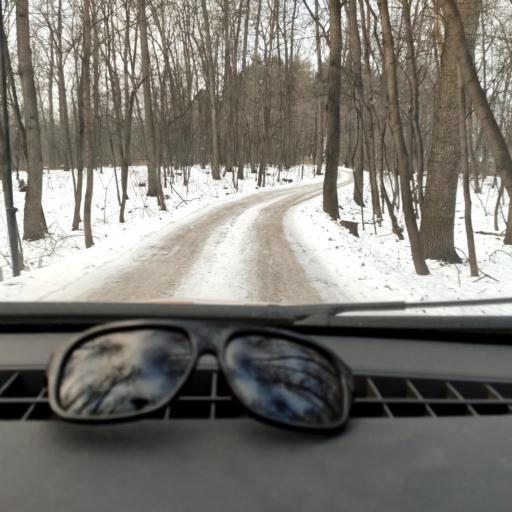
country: RU
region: Bashkortostan
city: Ufa
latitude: 54.7459
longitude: 56.0080
